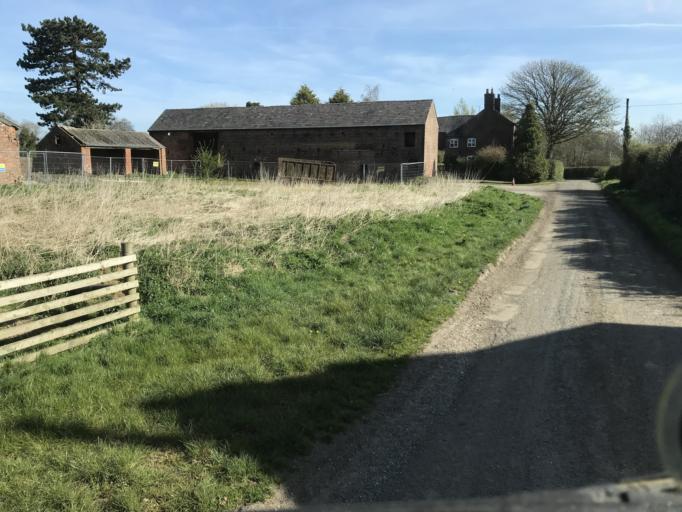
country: GB
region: England
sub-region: Cheshire West and Chester
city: Marston
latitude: 53.2263
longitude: -2.4769
